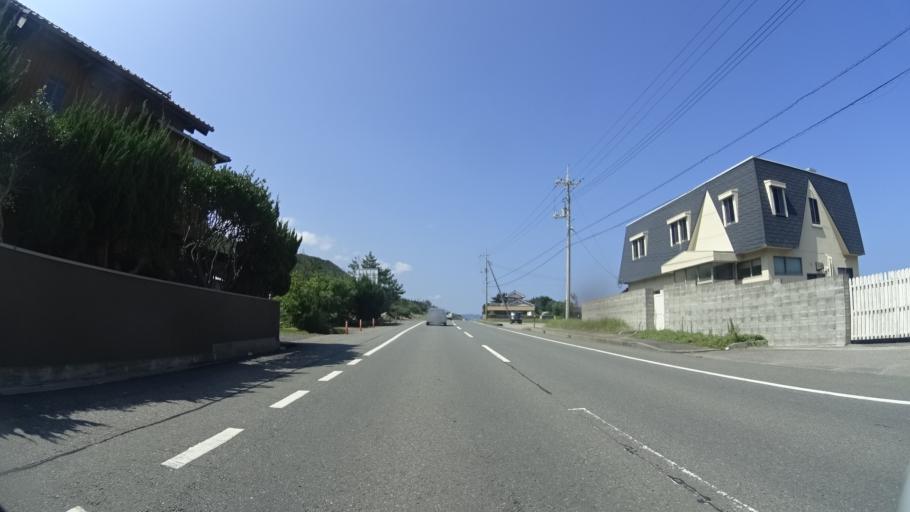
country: JP
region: Shimane
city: Masuda
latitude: 34.6867
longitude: 131.7942
